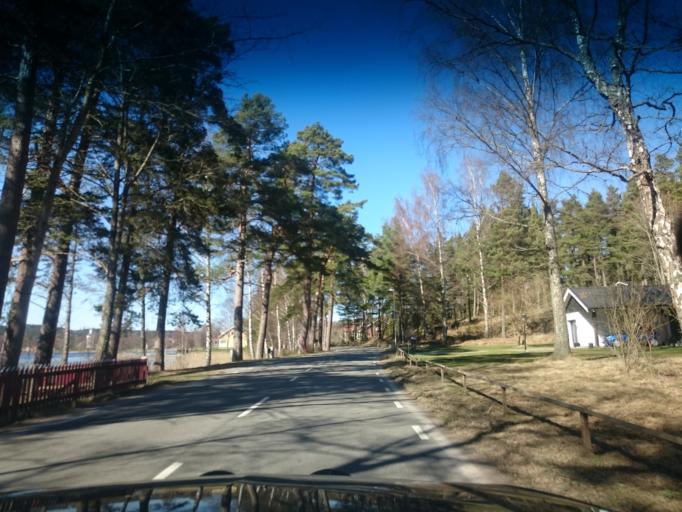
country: SE
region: Kronoberg
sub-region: Vaxjo Kommun
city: Braas
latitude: 57.1999
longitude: 14.9578
